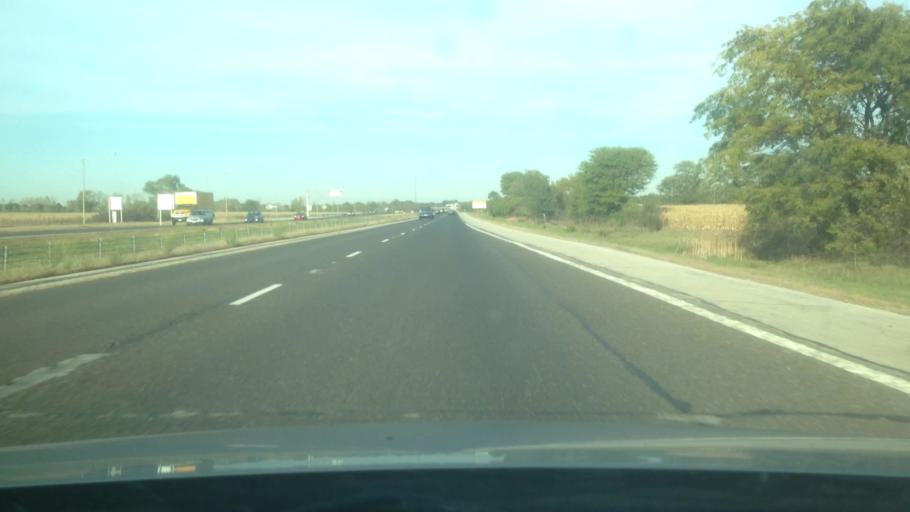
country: US
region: Illinois
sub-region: Will County
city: Peotone
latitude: 41.3668
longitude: -87.7977
